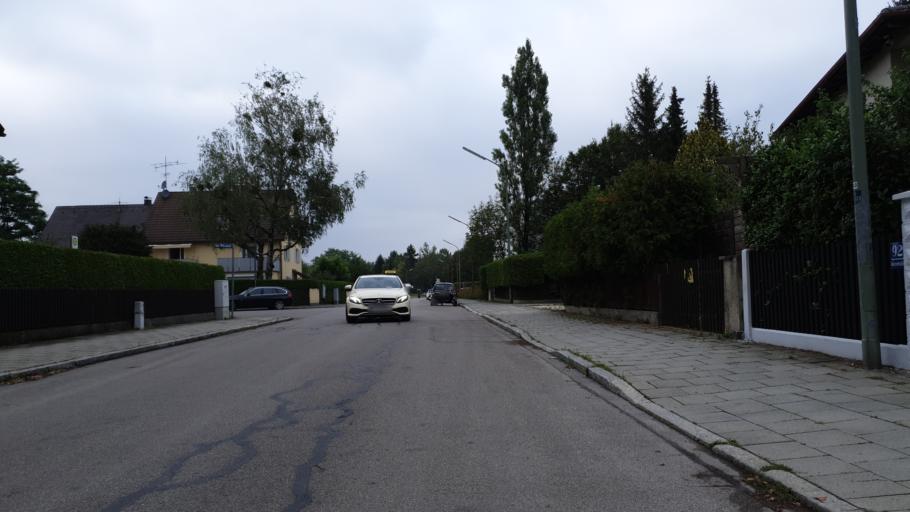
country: DE
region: Bavaria
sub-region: Upper Bavaria
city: Pasing
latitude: 48.1746
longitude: 11.4730
